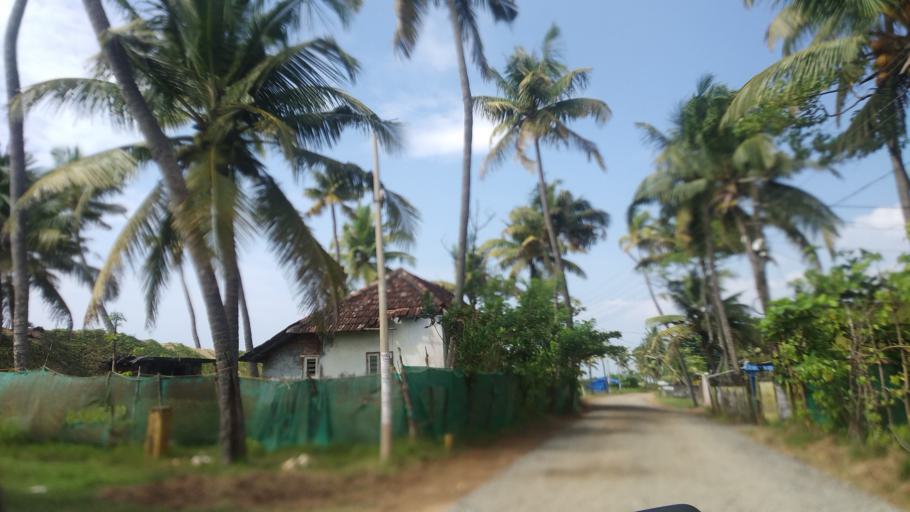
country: IN
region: Kerala
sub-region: Ernakulam
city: Elur
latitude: 10.0597
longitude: 76.2004
